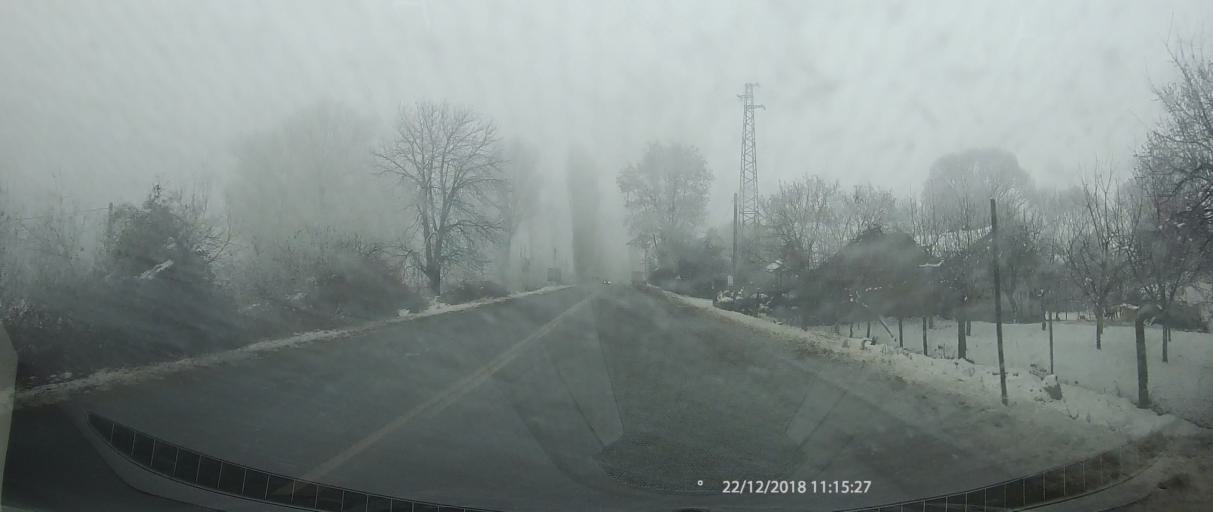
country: BG
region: Kyustendil
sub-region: Obshtina Kyustendil
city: Kyustendil
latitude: 42.2813
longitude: 22.7232
